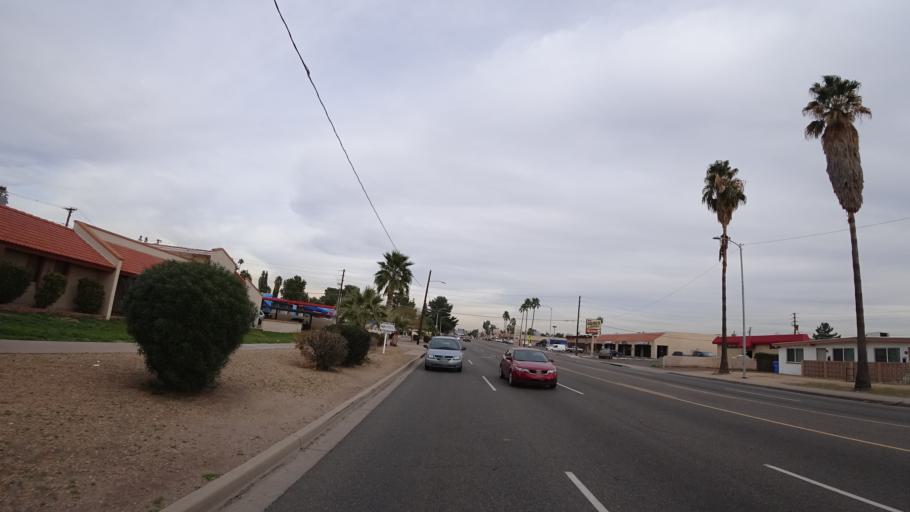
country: US
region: Arizona
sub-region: Maricopa County
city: Glendale
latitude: 33.5676
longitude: -112.1373
